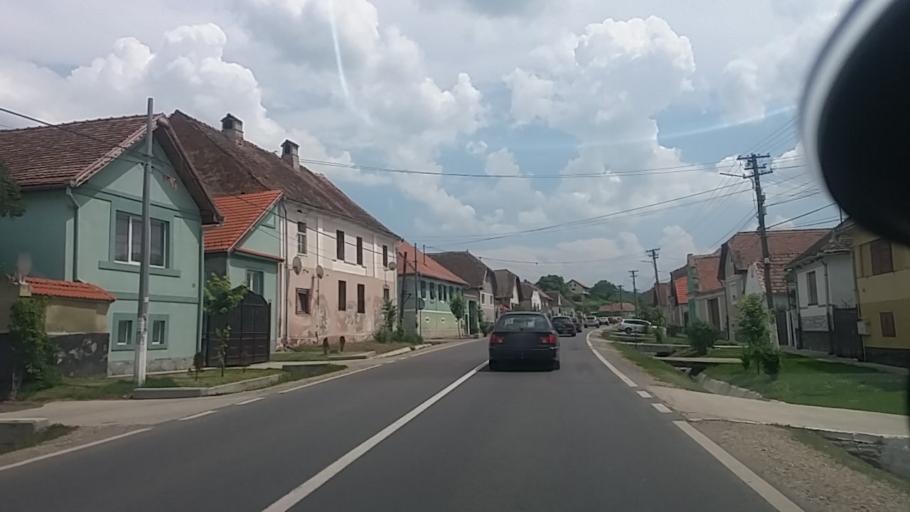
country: RO
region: Sibiu
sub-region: Comuna Slimnic
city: Slimnic
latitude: 45.9567
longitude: 24.1691
